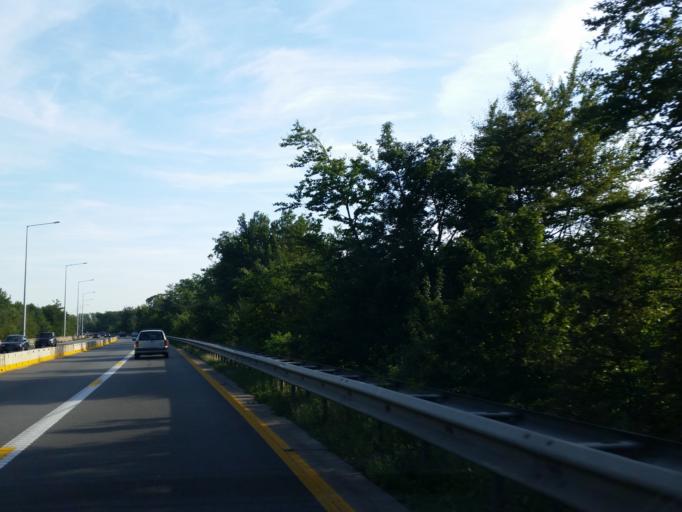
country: BE
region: Flanders
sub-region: Provincie Antwerpen
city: Mechelen
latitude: 51.0309
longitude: 4.4472
